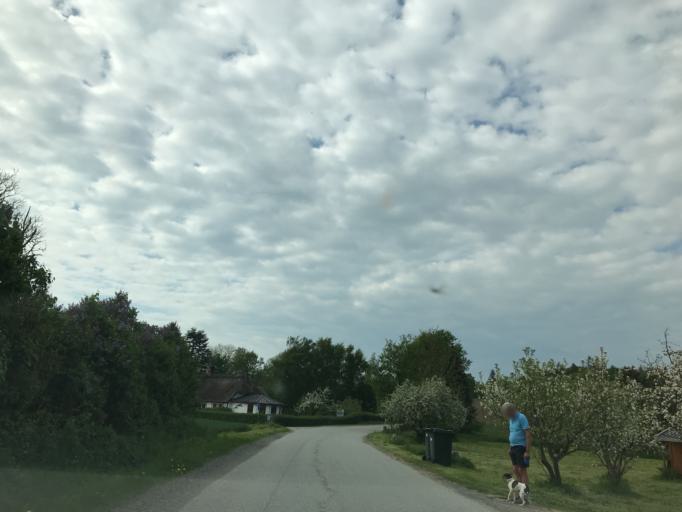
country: DK
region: South Denmark
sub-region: Assens Kommune
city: Assens
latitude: 55.3321
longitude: 9.9143
